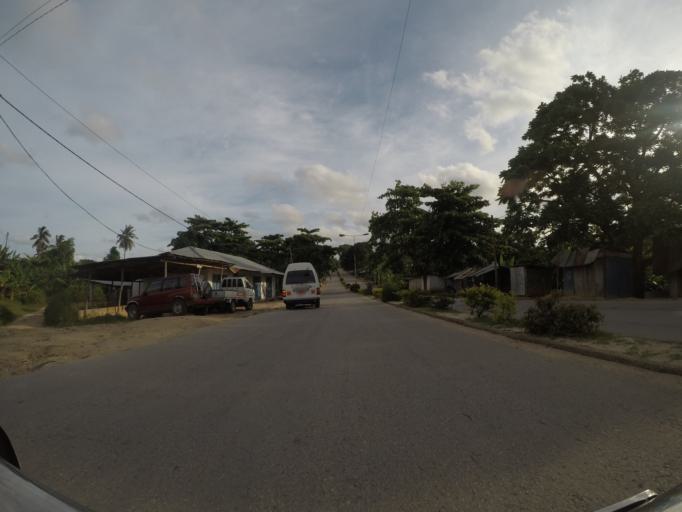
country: TZ
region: Pemba South
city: Chake Chake
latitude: -5.2532
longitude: 39.7750
